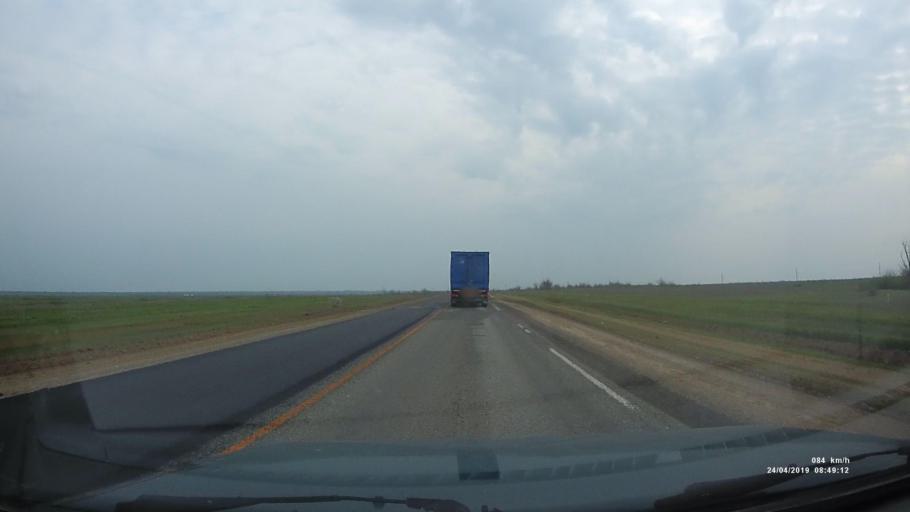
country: RU
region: Kalmykiya
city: Arshan'
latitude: 46.2556
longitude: 44.1207
